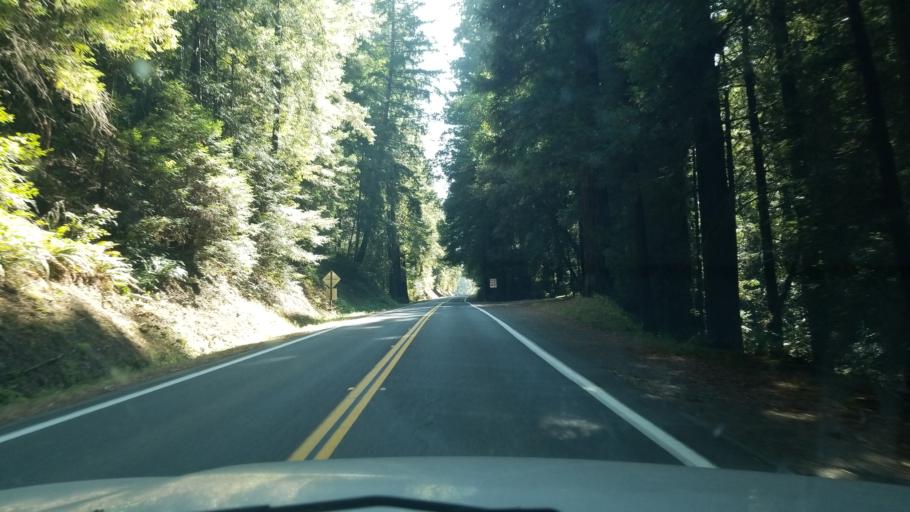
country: US
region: California
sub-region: Humboldt County
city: Redway
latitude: 40.2415
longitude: -123.8213
